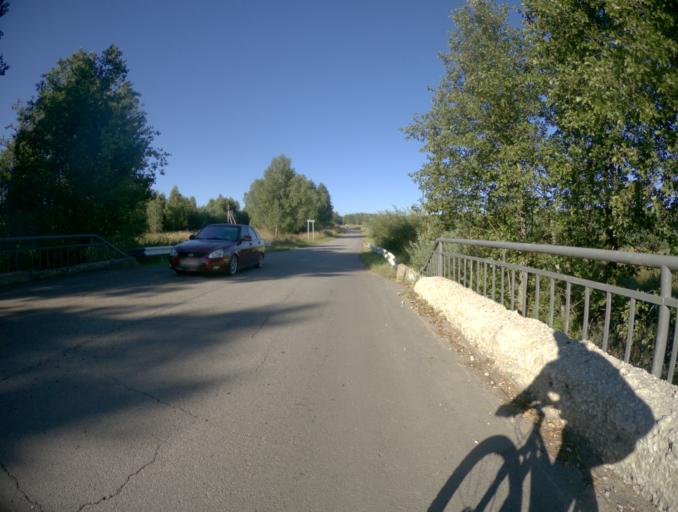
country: RU
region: Vladimir
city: Nikologory
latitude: 56.2058
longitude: 41.9750
